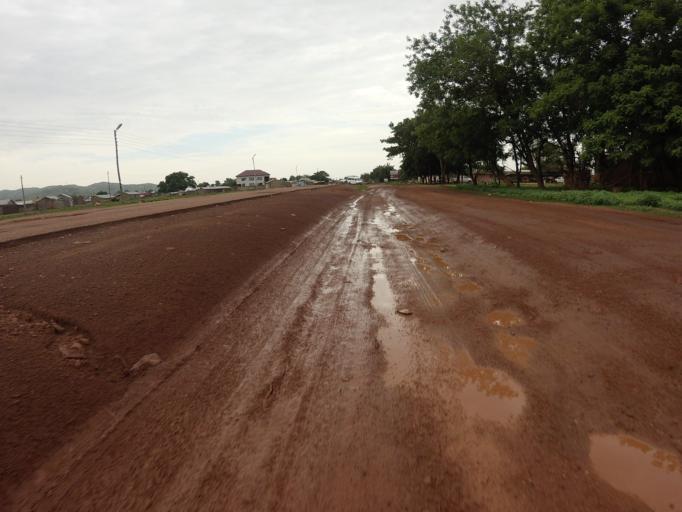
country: GH
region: Upper East
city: Bawku
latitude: 10.9316
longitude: -0.5013
